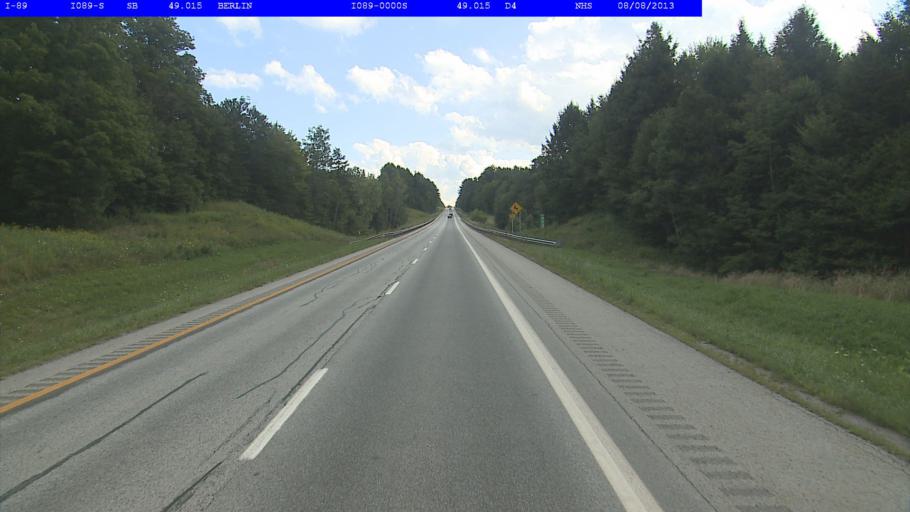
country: US
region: Vermont
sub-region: Washington County
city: Montpelier
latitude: 44.1980
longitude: -72.5777
